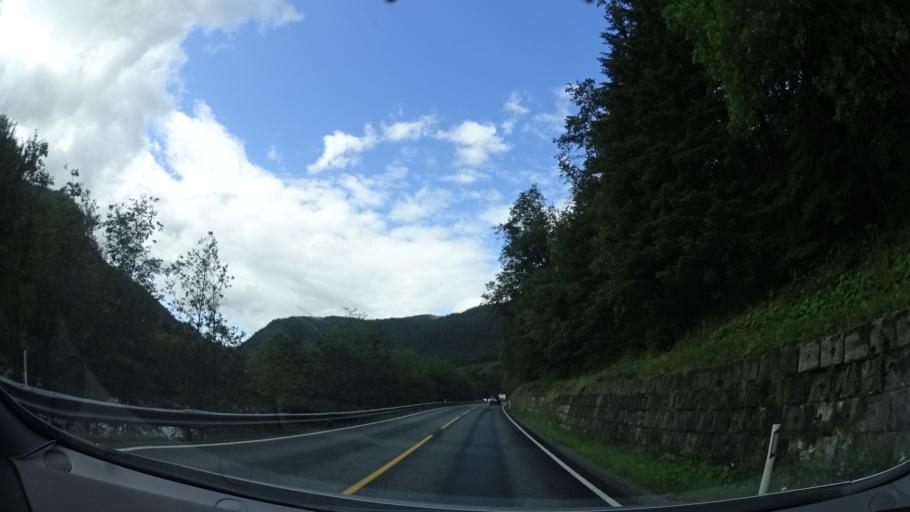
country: NO
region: Nord-Trondelag
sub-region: Meraker
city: Meraker
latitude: 63.4513
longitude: 11.5855
